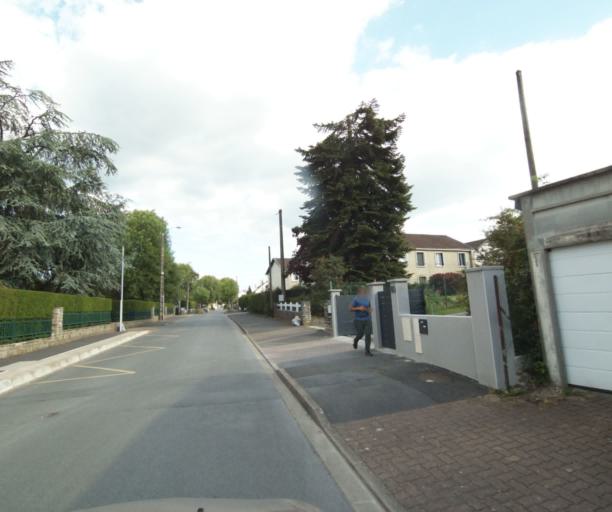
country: FR
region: Champagne-Ardenne
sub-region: Departement des Ardennes
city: Montcy-Notre-Dame
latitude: 49.7809
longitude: 4.7291
